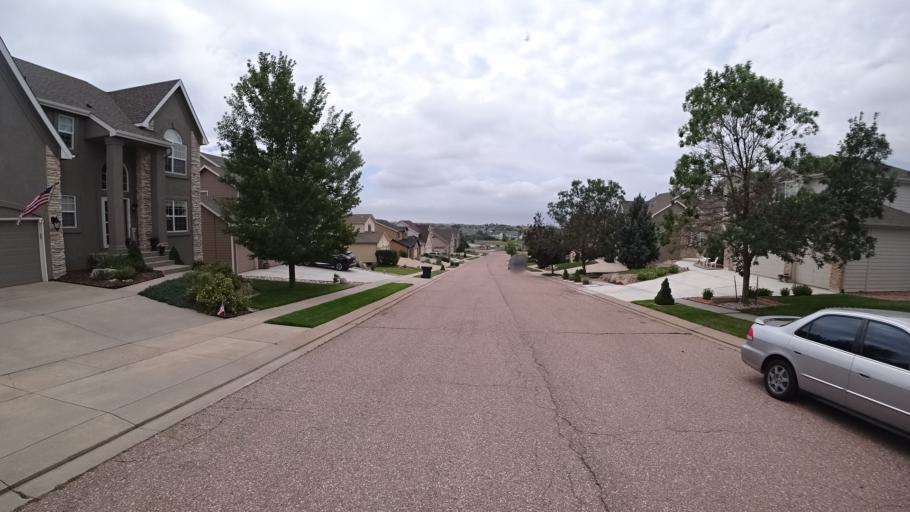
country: US
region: Colorado
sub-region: El Paso County
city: Gleneagle
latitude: 39.0143
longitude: -104.8047
